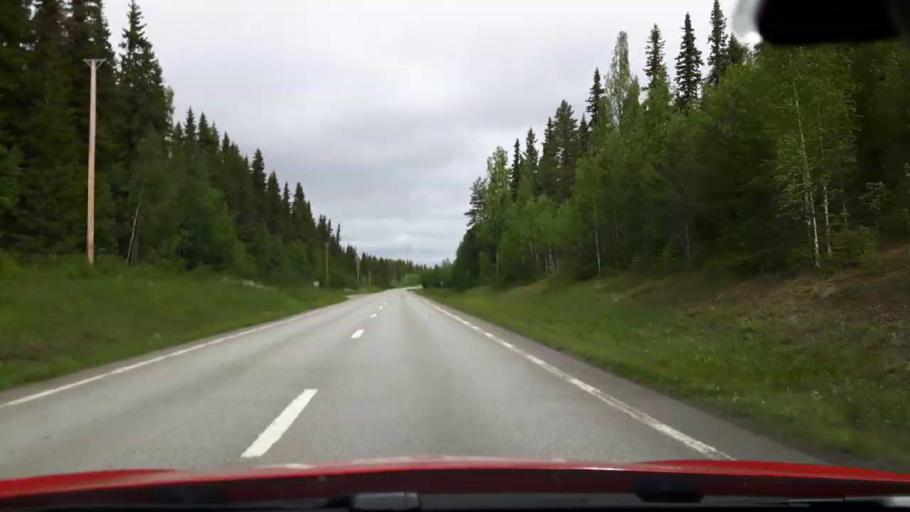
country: SE
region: Jaemtland
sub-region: Krokoms Kommun
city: Krokom
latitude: 63.4900
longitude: 14.5064
